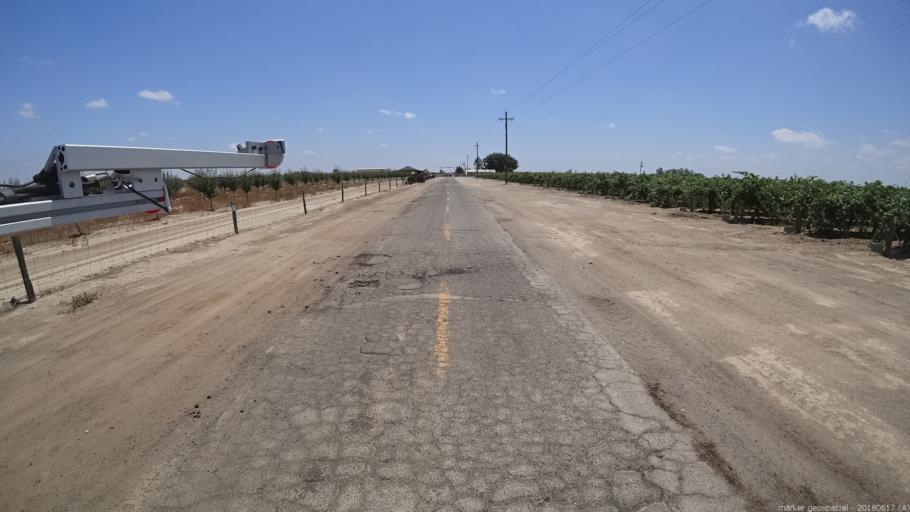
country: US
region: California
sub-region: Fresno County
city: Kerman
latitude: 36.8095
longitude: -120.1508
